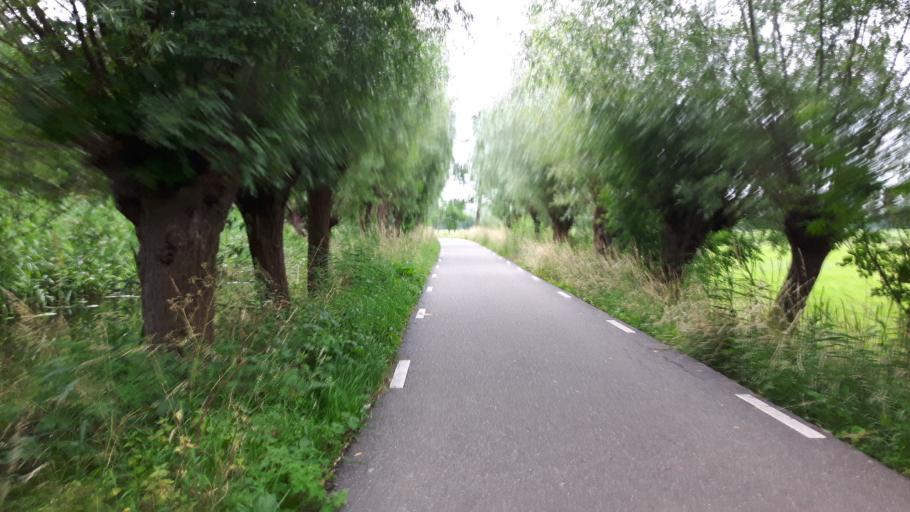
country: NL
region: Utrecht
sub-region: Gemeente Woerden
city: Woerden
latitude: 52.0573
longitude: 4.8946
